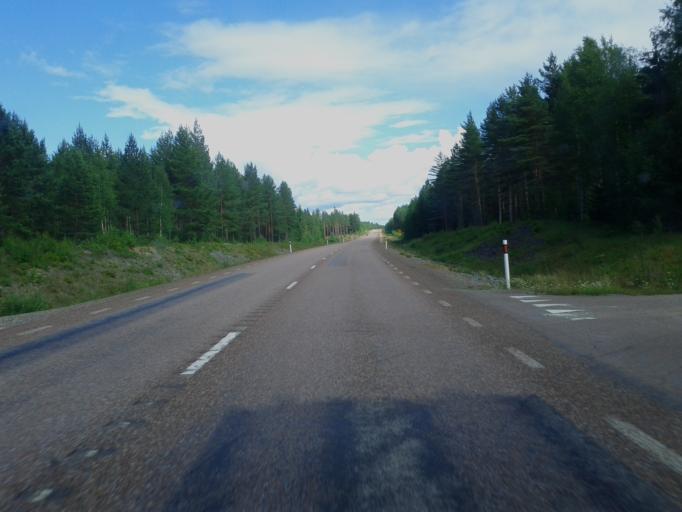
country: SE
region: Dalarna
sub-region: Rattviks Kommun
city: Raettvik
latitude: 60.8458
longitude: 15.1580
